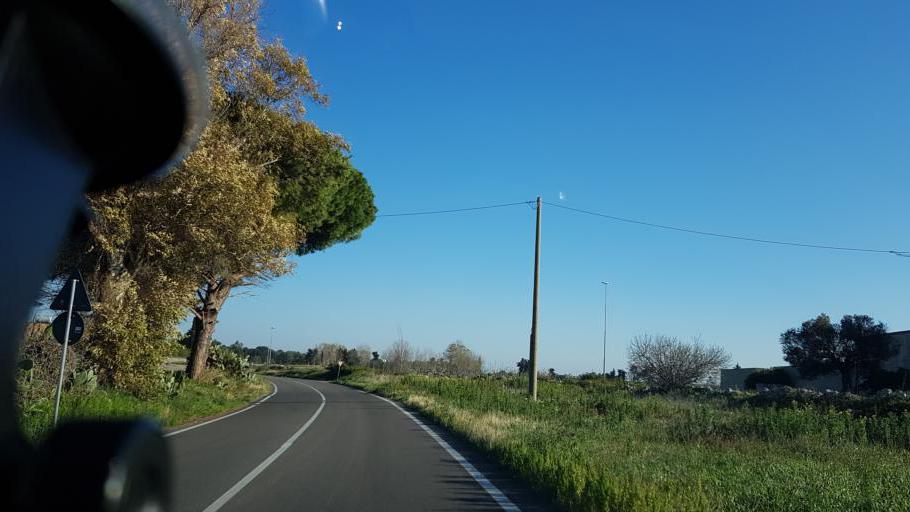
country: IT
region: Apulia
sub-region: Provincia di Lecce
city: Merine
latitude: 40.4124
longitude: 18.2546
